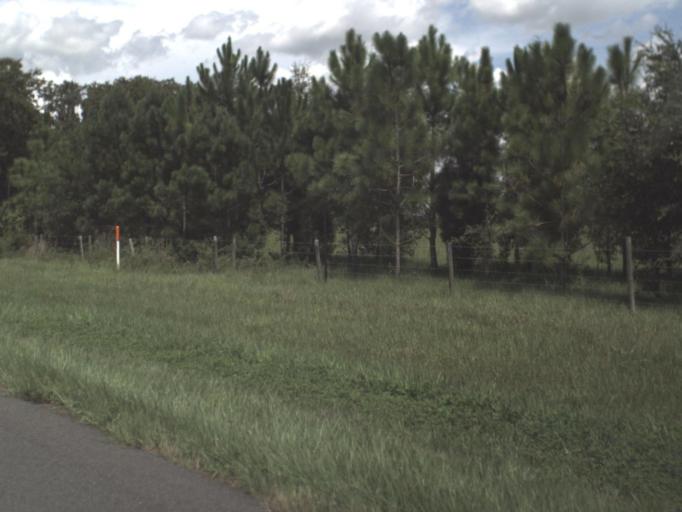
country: US
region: Florida
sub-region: Hillsborough County
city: Balm
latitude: 27.7045
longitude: -82.1587
